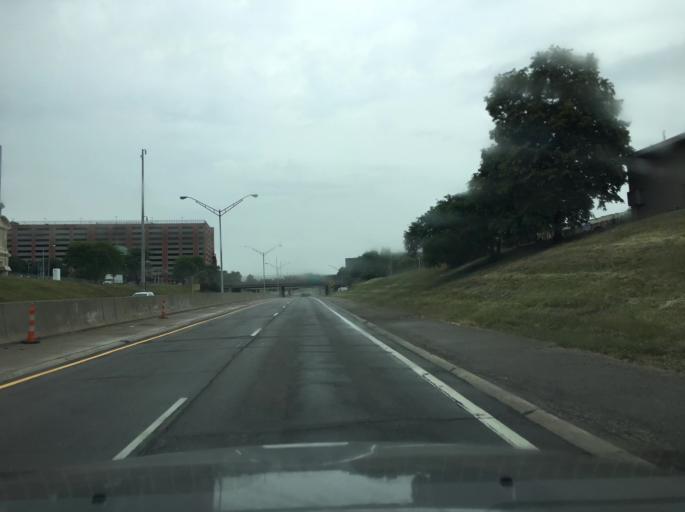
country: US
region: Michigan
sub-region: Wayne County
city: Detroit
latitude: 42.3337
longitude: -83.0364
